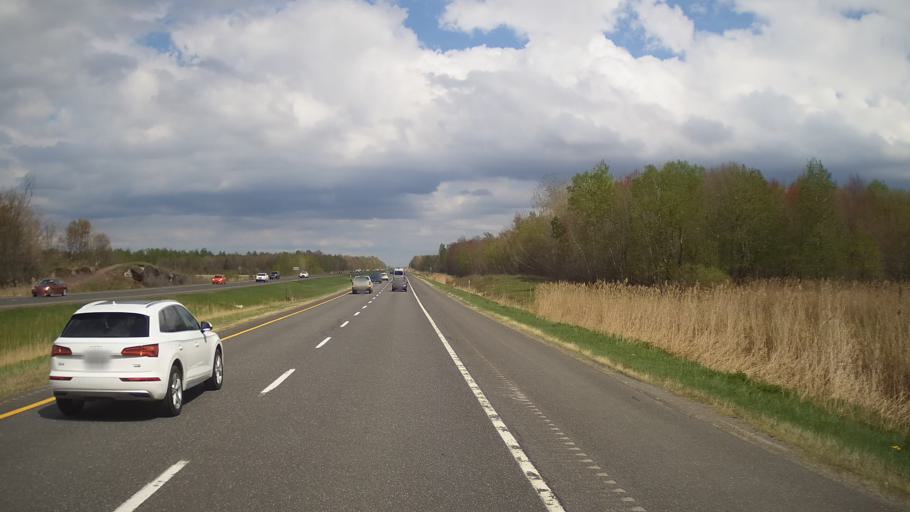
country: CA
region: Quebec
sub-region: Monteregie
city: Farnham
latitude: 45.3568
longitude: -72.8912
